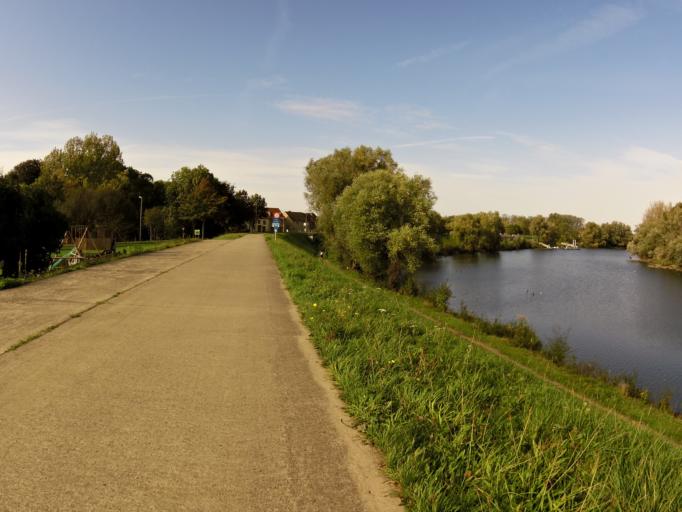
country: NL
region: Limburg
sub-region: Gemeente Stein
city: Berg
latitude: 51.0202
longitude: 5.7518
